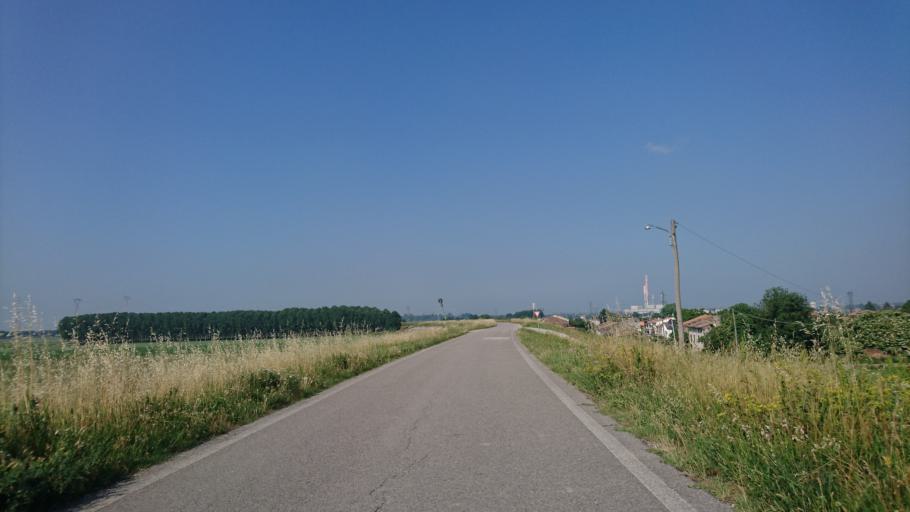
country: IT
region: Veneto
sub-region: Provincia di Rovigo
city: Melara
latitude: 45.0601
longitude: 11.1733
